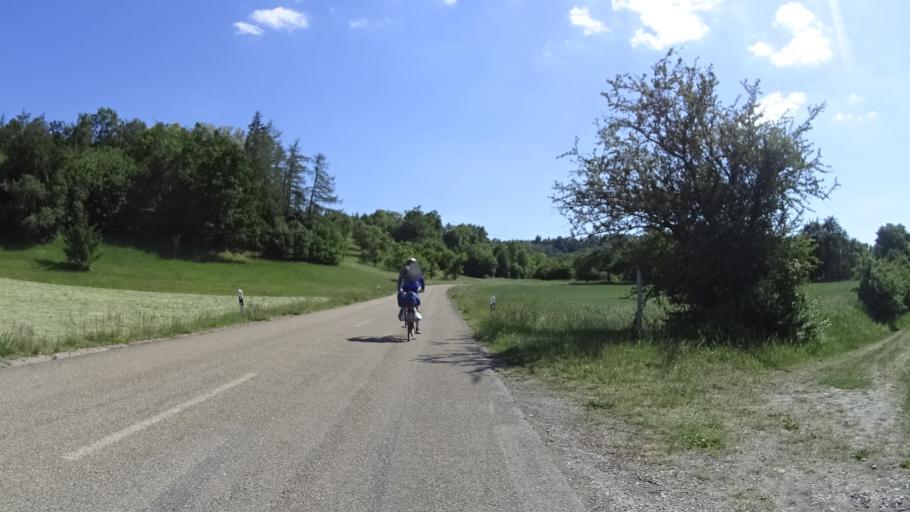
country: DE
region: Bavaria
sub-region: Regierungsbezirk Mittelfranken
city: Diebach
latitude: 49.2747
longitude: 10.2152
